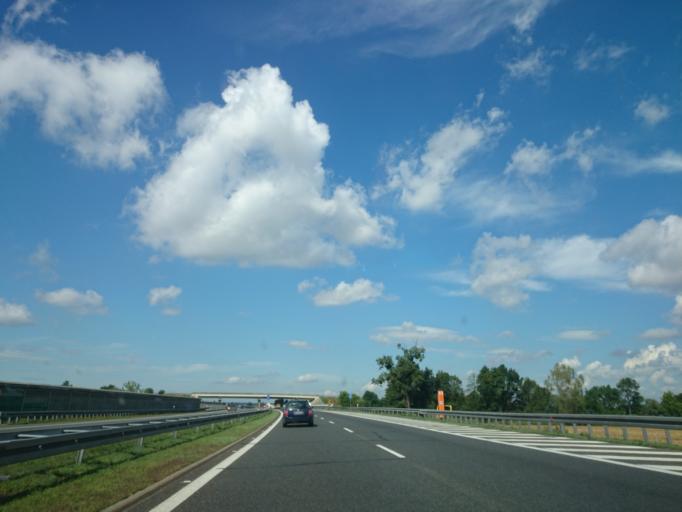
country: PL
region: Opole Voivodeship
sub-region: Powiat brzeski
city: Lewin Brzeski
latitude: 50.7087
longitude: 17.6051
